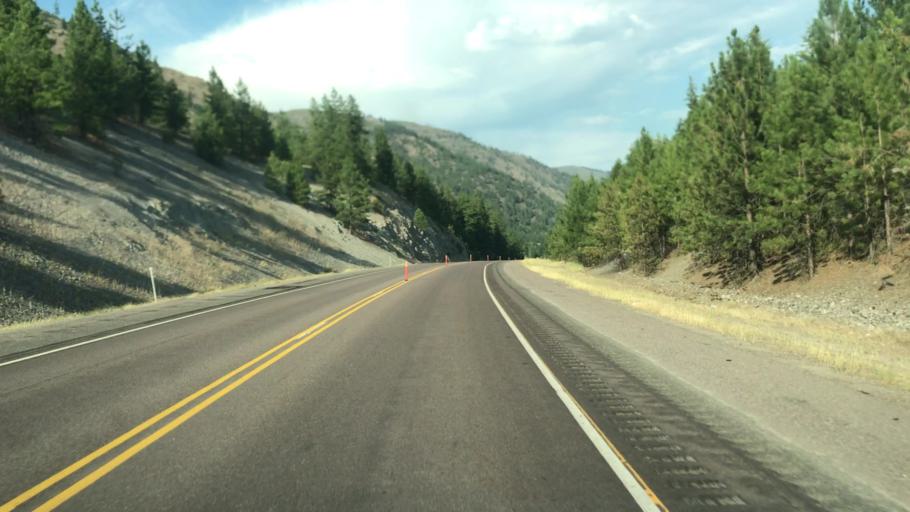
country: US
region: Montana
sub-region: Mineral County
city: Superior
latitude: 47.0162
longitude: -114.6898
